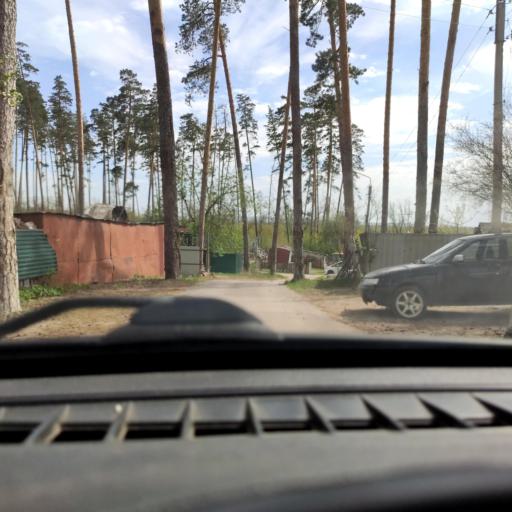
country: RU
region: Samara
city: Tol'yatti
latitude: 53.5001
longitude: 49.3544
